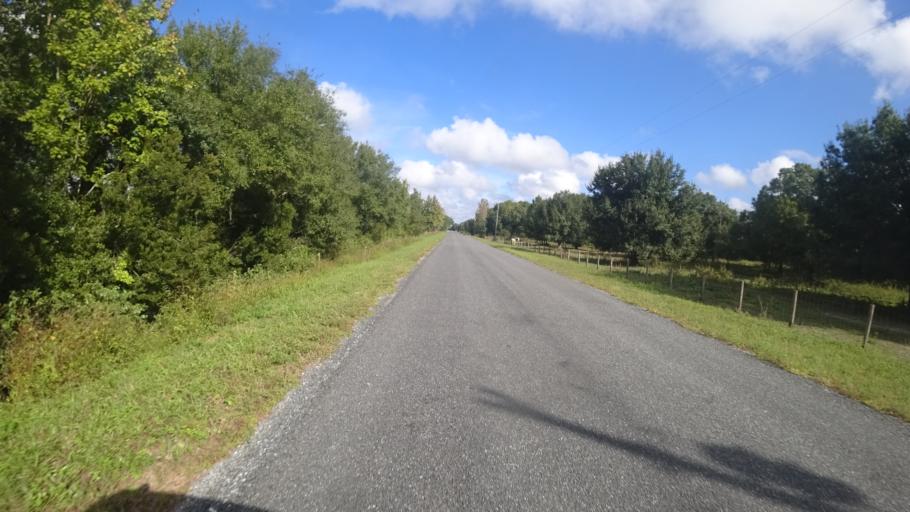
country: US
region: Florida
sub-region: Hillsborough County
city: Wimauma
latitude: 27.4677
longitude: -82.1533
